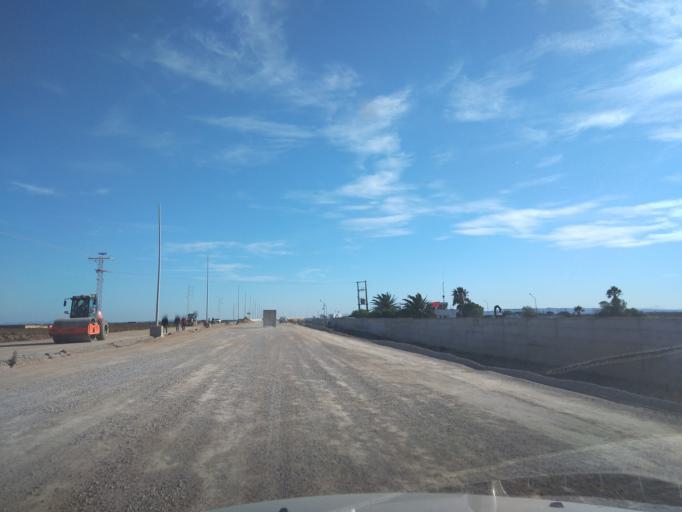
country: TN
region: Ariana
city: Qal'at al Andalus
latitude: 37.0433
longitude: 10.1284
